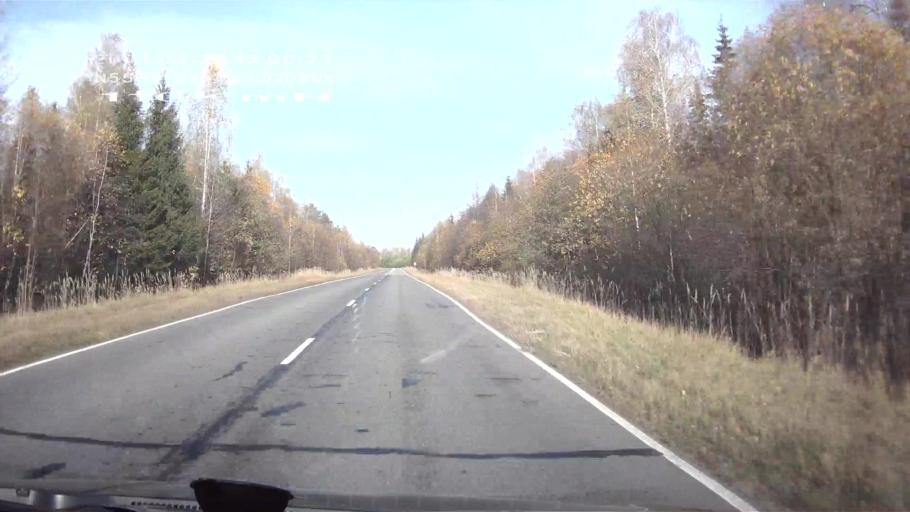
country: RU
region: Chuvashia
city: Buinsk
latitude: 55.1877
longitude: 47.0709
